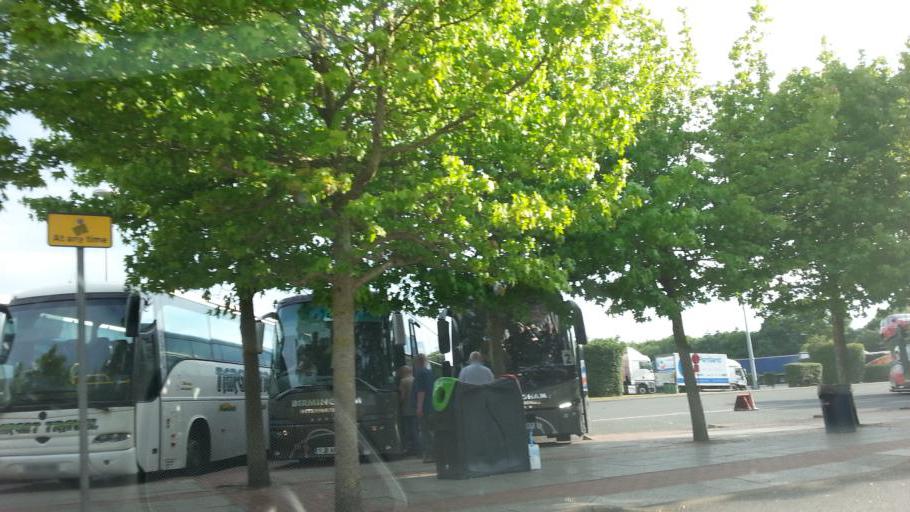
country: GB
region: England
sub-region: Worcestershire
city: Bredon
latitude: 52.0651
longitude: -2.1578
